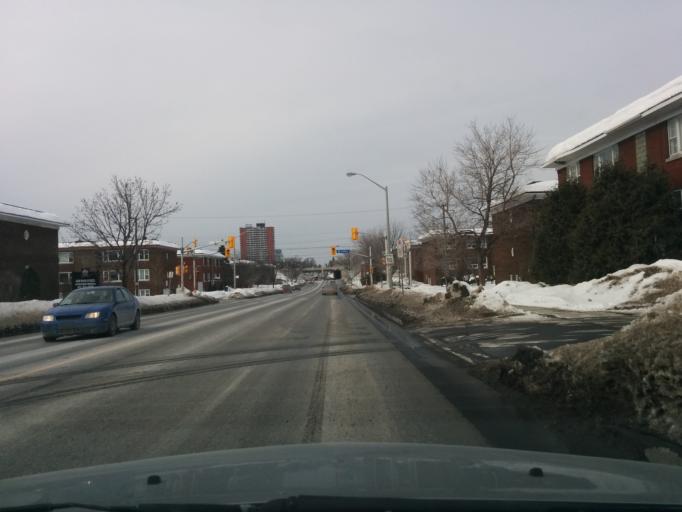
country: CA
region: Ontario
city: Ottawa
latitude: 45.3811
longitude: -75.7380
